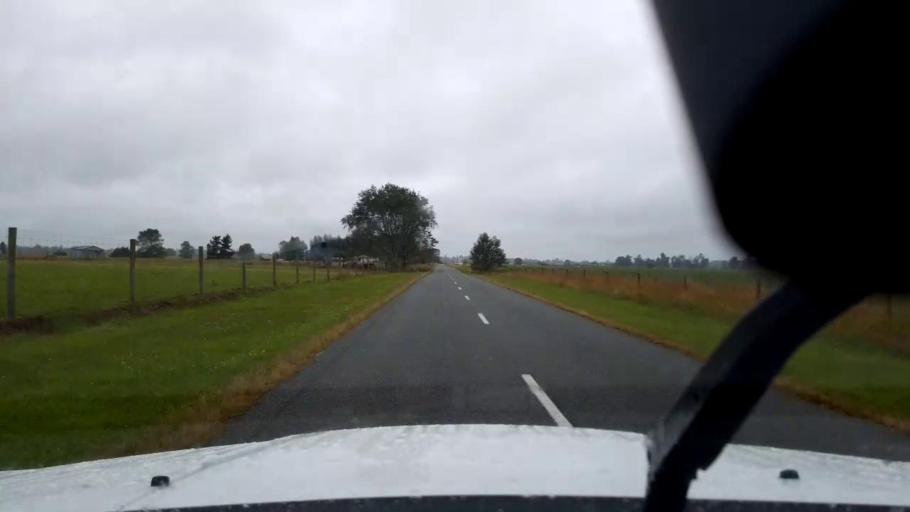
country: NZ
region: Canterbury
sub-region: Timaru District
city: Pleasant Point
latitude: -44.2516
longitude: 171.2250
